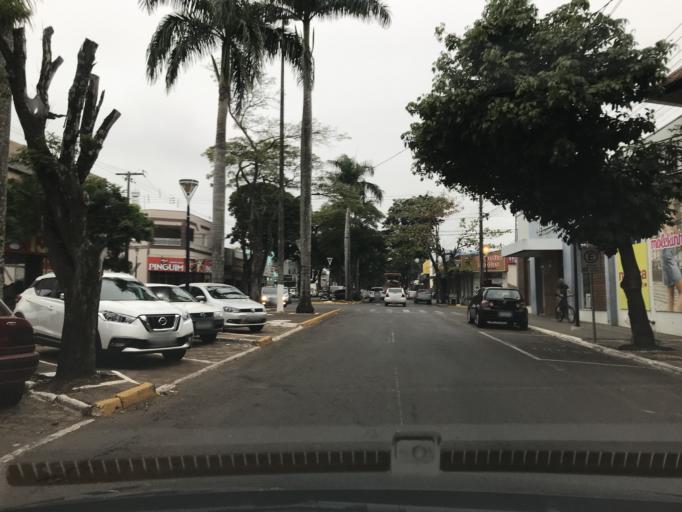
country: PY
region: Canindeyu
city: Salto del Guaira
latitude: -24.0828
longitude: -54.2475
